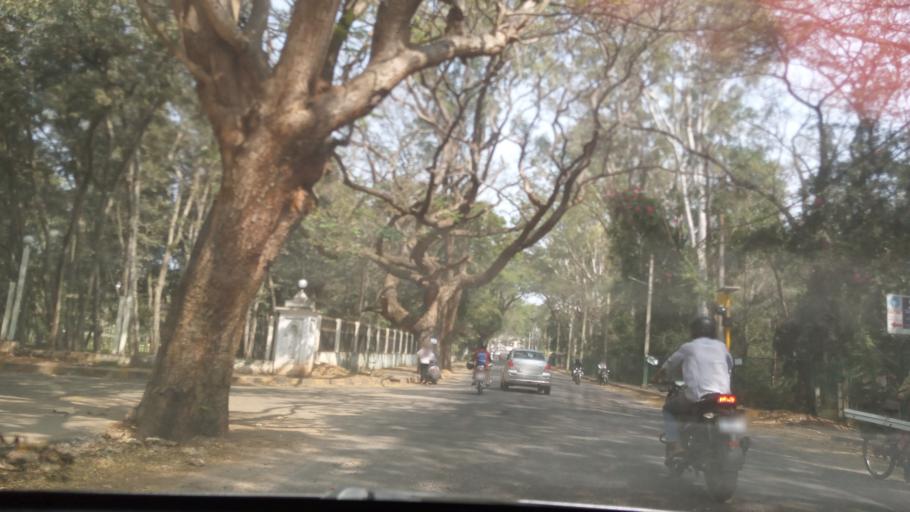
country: IN
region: Karnataka
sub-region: Mysore
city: Mysore
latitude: 12.3137
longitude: 76.6271
